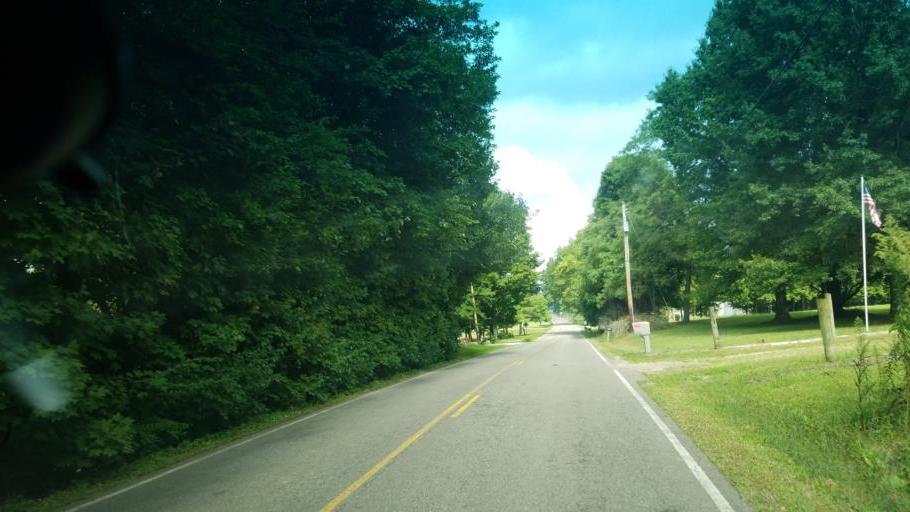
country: US
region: Ohio
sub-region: Licking County
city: Johnstown
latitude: 40.1976
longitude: -82.6032
